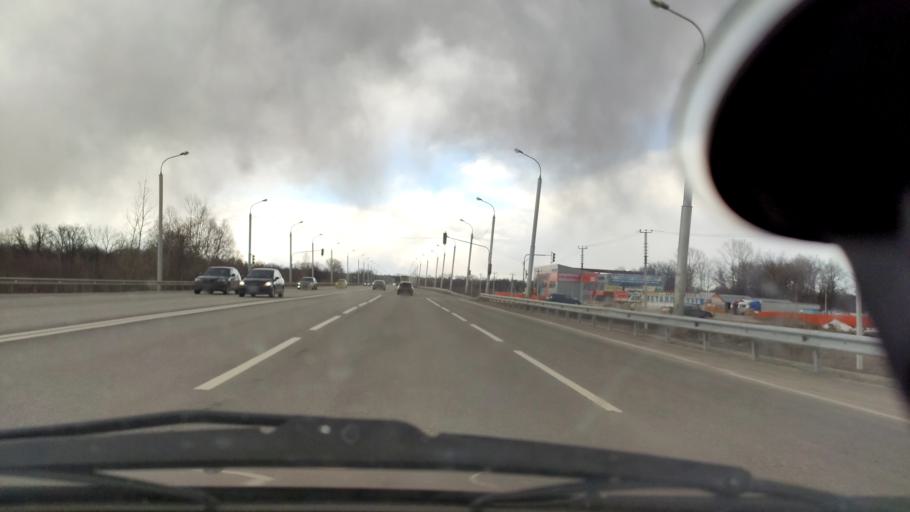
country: RU
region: Bashkortostan
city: Ufa
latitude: 54.8057
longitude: 56.1835
